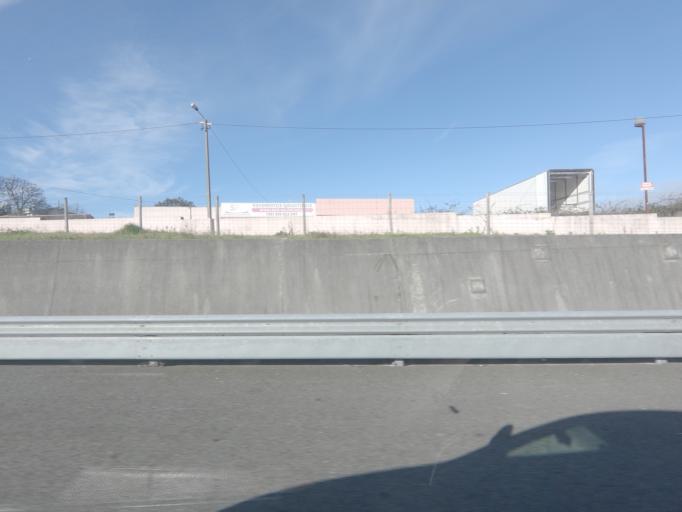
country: PT
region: Aveiro
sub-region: Santa Maria da Feira
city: Feira
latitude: 40.9068
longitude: -8.5673
